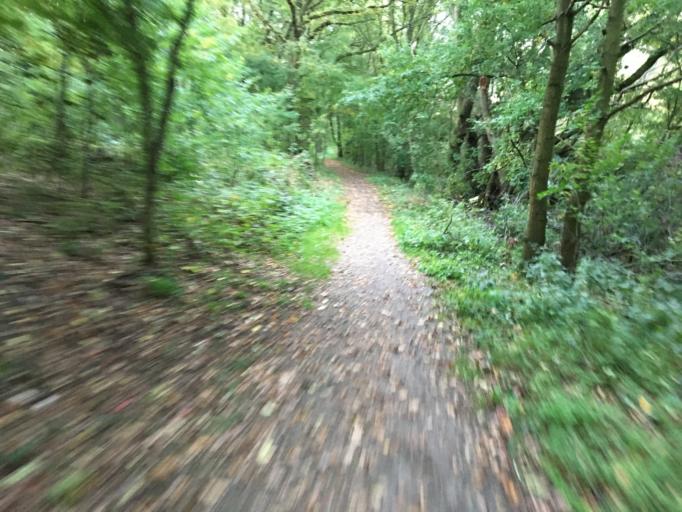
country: DE
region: Lower Saxony
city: Braunschweig
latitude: 52.2991
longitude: 10.5392
